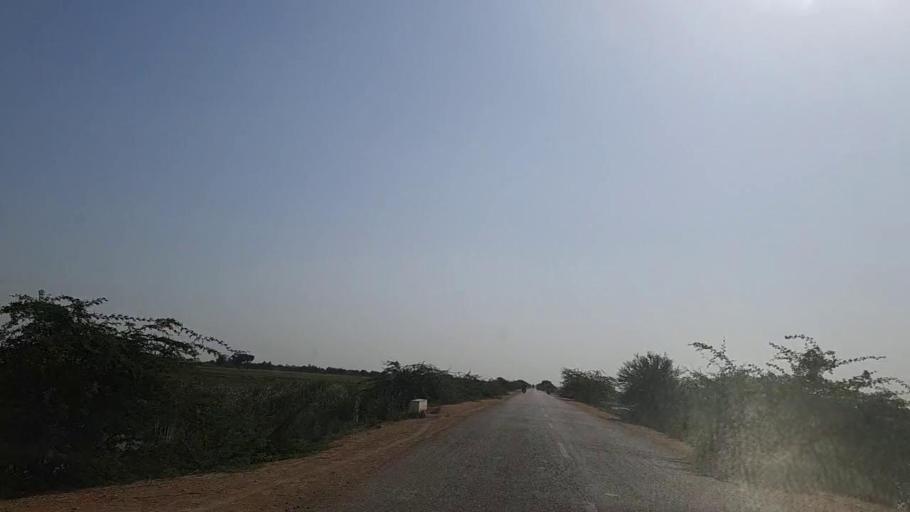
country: PK
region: Sindh
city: Mirpur Batoro
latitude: 24.5893
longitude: 68.2916
